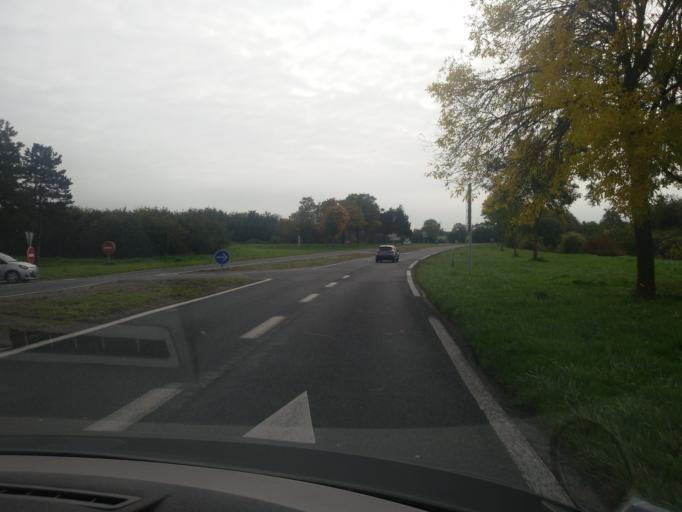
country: FR
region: Lower Normandy
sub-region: Departement du Calvados
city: Dives-sur-Mer
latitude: 49.2720
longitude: -0.1039
